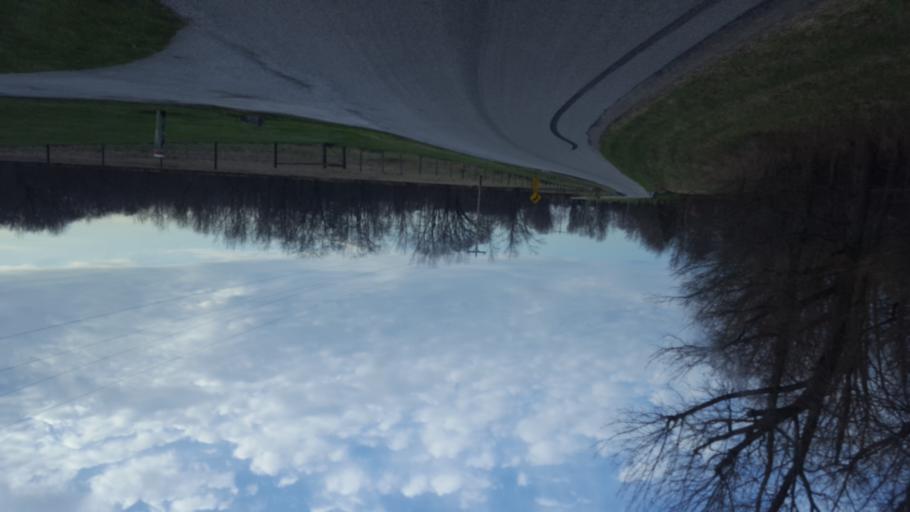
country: US
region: Ohio
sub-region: Crawford County
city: Bucyrus
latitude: 40.6611
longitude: -82.9489
